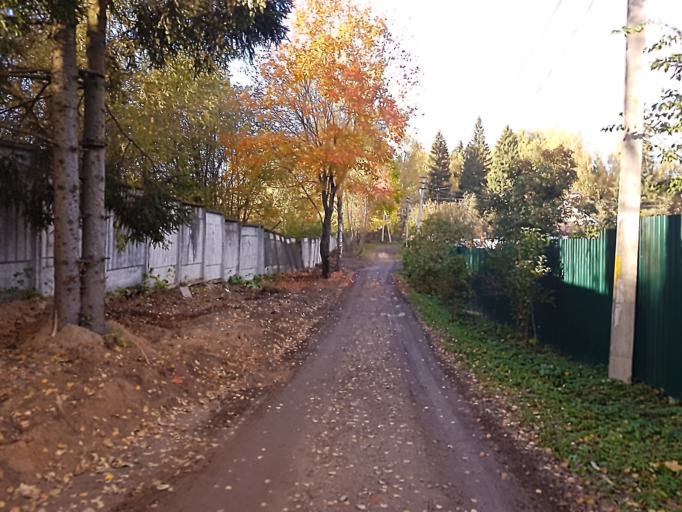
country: RU
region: Moskovskaya
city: Istra
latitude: 55.9179
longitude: 36.8829
